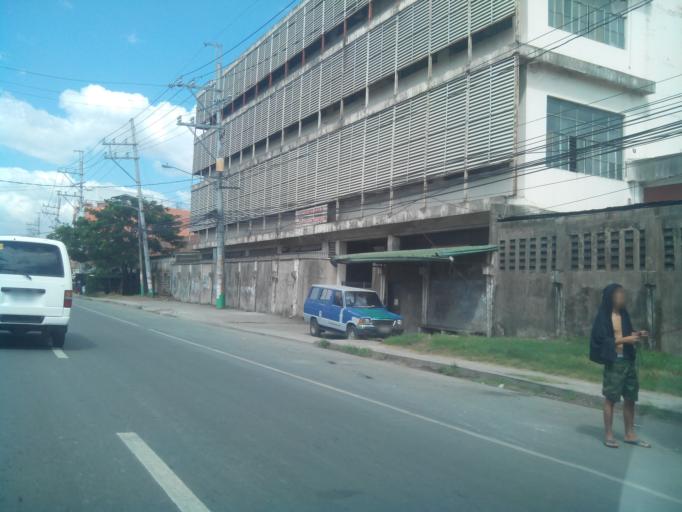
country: PH
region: Calabarzon
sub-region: Province of Rizal
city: Taytay
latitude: 14.5503
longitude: 121.1401
